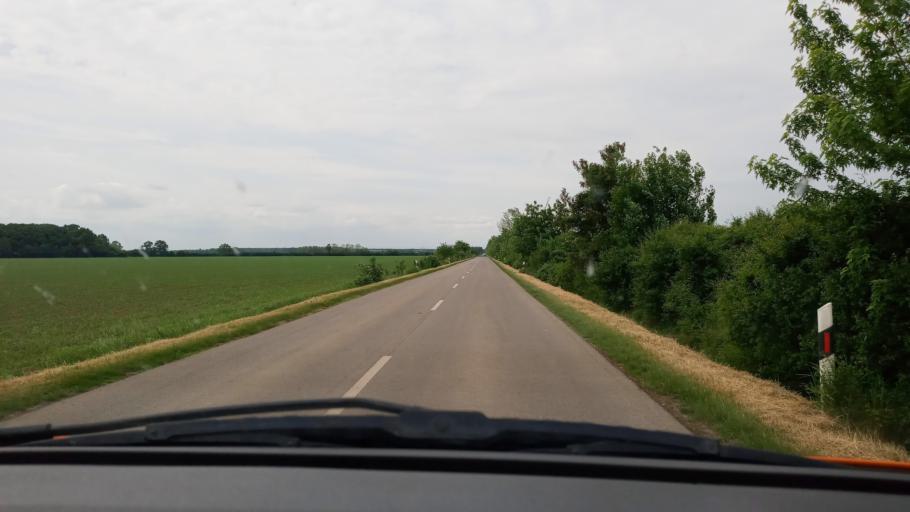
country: HU
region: Baranya
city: Vajszlo
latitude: 45.9236
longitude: 18.0604
